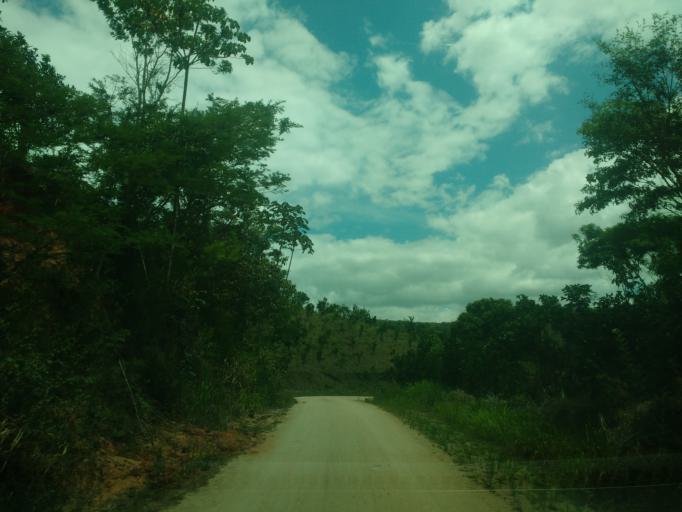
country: BR
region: Alagoas
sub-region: Santana Do Mundau
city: Santana do Mundau
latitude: -9.1573
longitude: -36.1602
